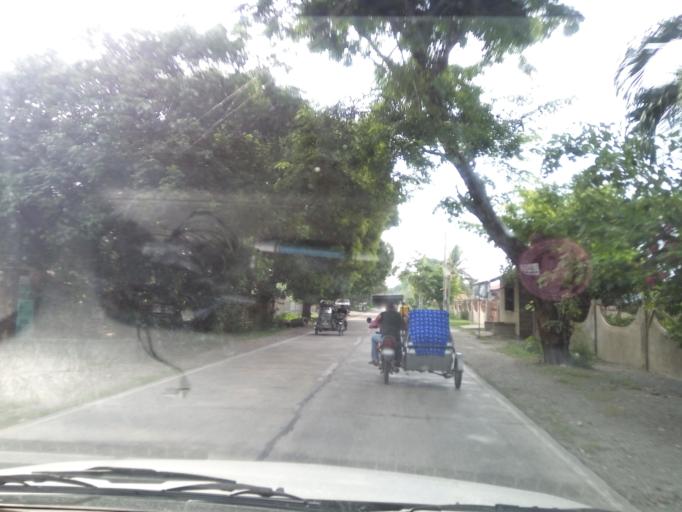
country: PH
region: Ilocos
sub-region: Province of Pangasinan
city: Binalonan
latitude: 16.0438
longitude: 120.5997
